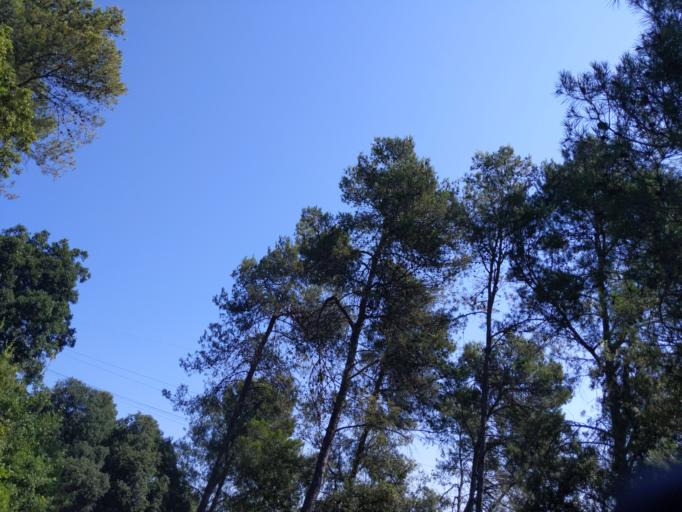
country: ES
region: Catalonia
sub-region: Provincia de Barcelona
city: Cerdanyola del Valles
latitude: 41.4598
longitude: 2.1366
